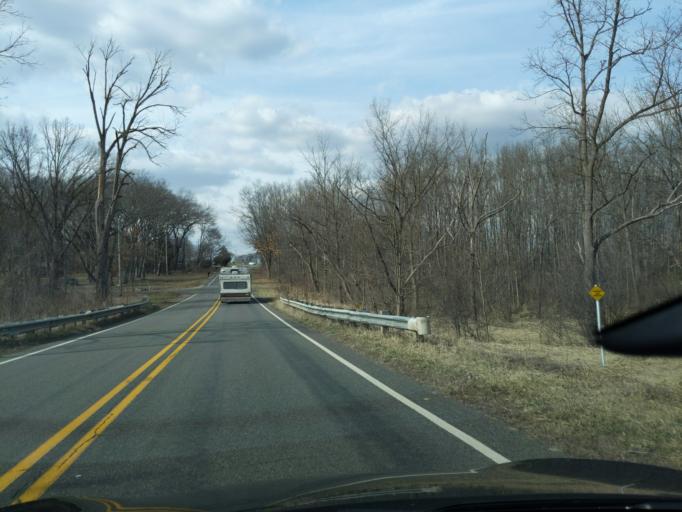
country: US
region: Michigan
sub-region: Ingham County
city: Leslie
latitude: 42.3543
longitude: -84.4175
